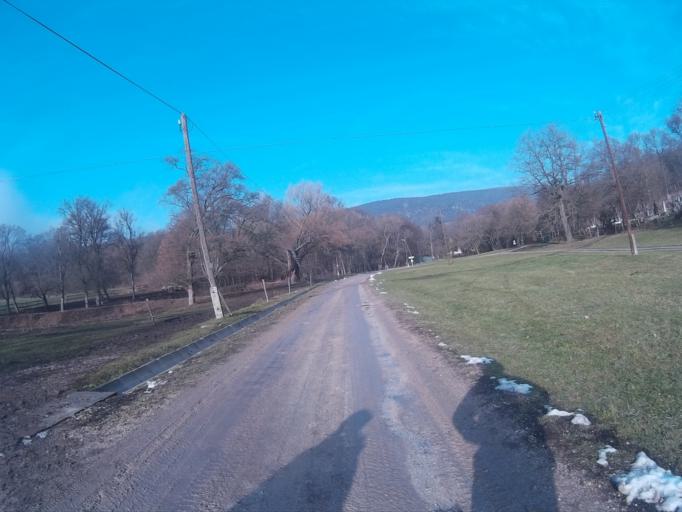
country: HU
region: Komarom-Esztergom
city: Tarjan
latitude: 47.6512
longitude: 18.5023
